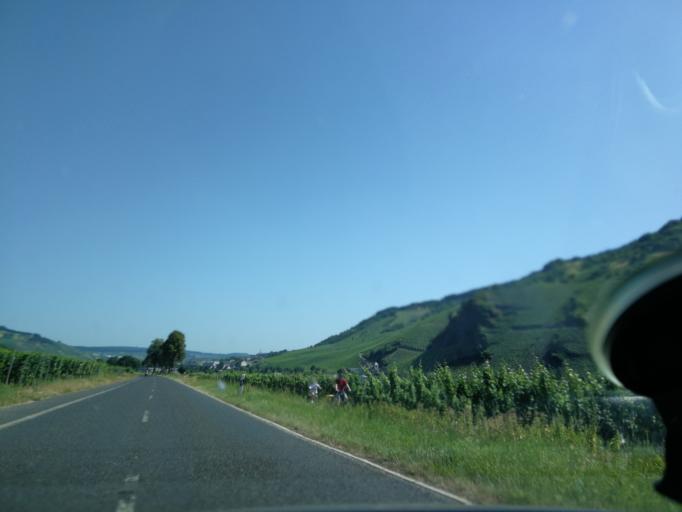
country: DE
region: Rheinland-Pfalz
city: Minheim
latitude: 49.8699
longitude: 6.9442
